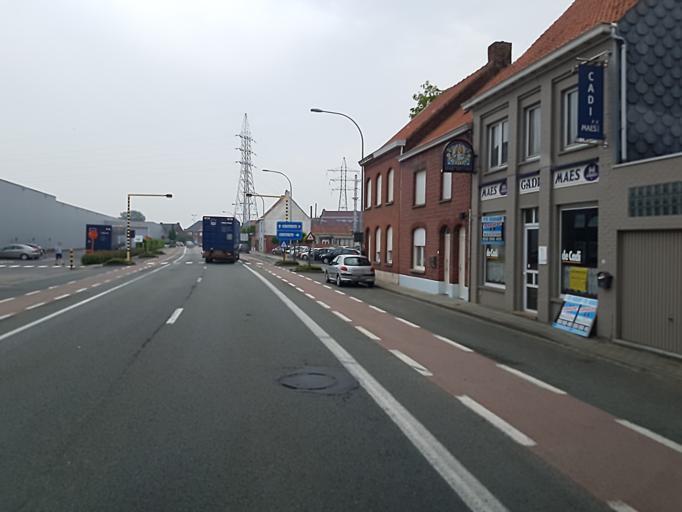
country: BE
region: Flanders
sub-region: Provincie West-Vlaanderen
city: Wielsbeke
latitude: 50.9123
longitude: 3.3963
